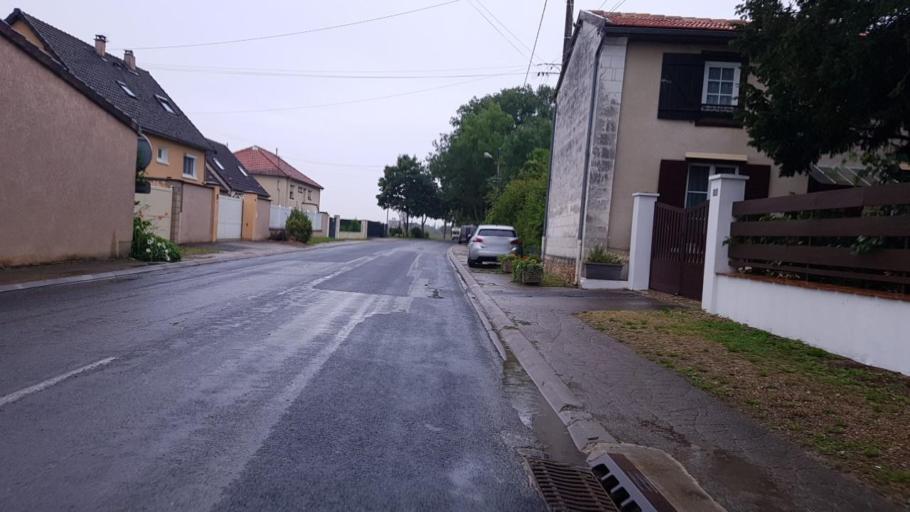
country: FR
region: Champagne-Ardenne
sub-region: Departement de la Marne
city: Sarry
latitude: 48.8737
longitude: 4.4586
